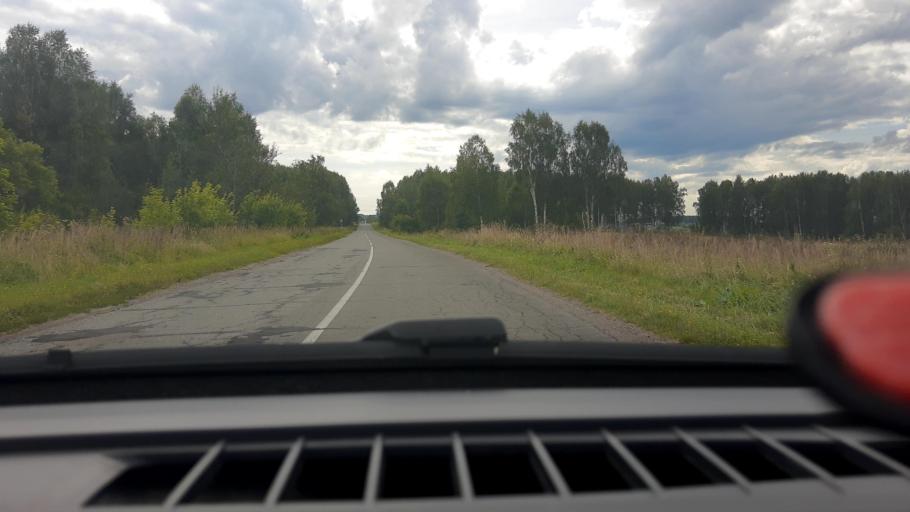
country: RU
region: Nizjnij Novgorod
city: Burevestnik
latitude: 56.0582
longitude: 43.6795
